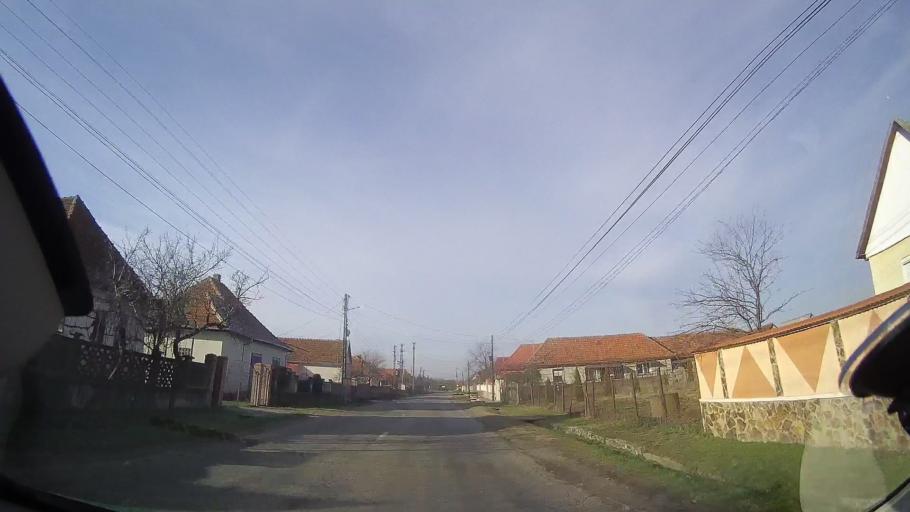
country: RO
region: Bihor
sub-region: Comuna Brusturi
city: Brusturi
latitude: 47.1528
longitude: 22.2468
